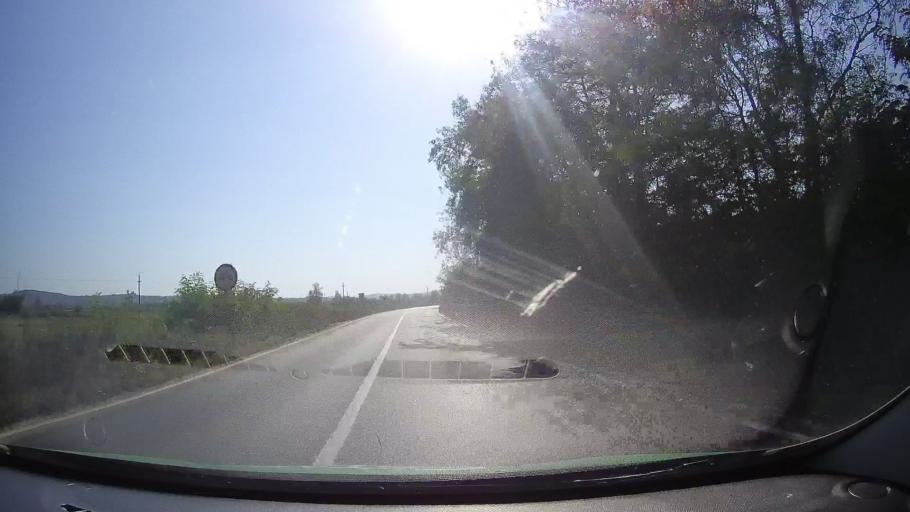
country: RO
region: Arad
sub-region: Comuna Ususau
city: Ususau
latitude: 46.1020
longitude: 21.8149
